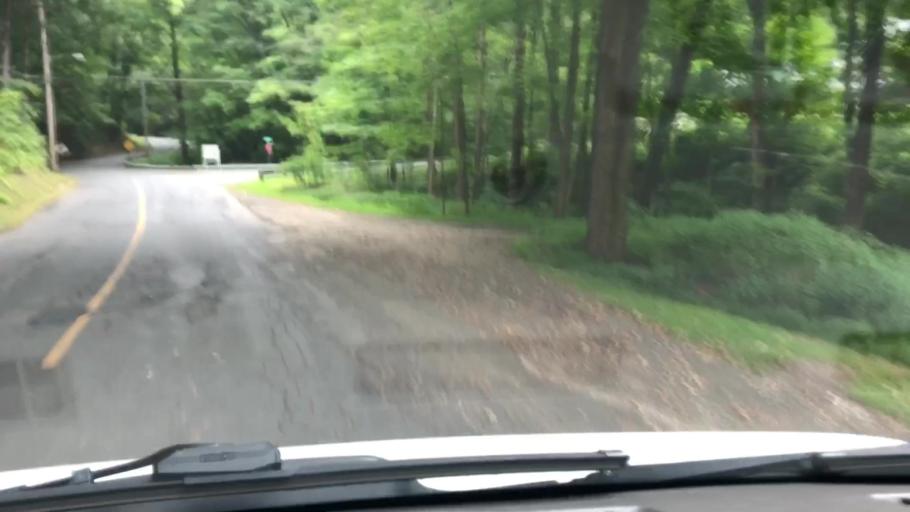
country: US
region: Massachusetts
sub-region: Franklin County
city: Greenfield
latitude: 42.5415
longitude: -72.5999
